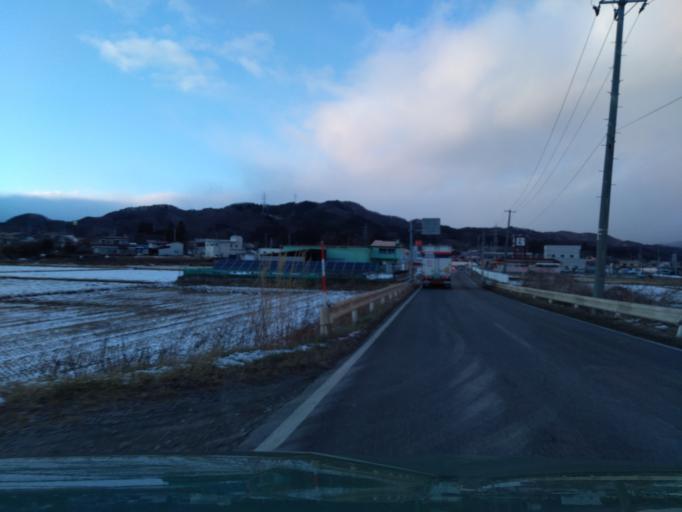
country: JP
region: Iwate
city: Shizukuishi
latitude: 39.6981
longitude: 141.0632
